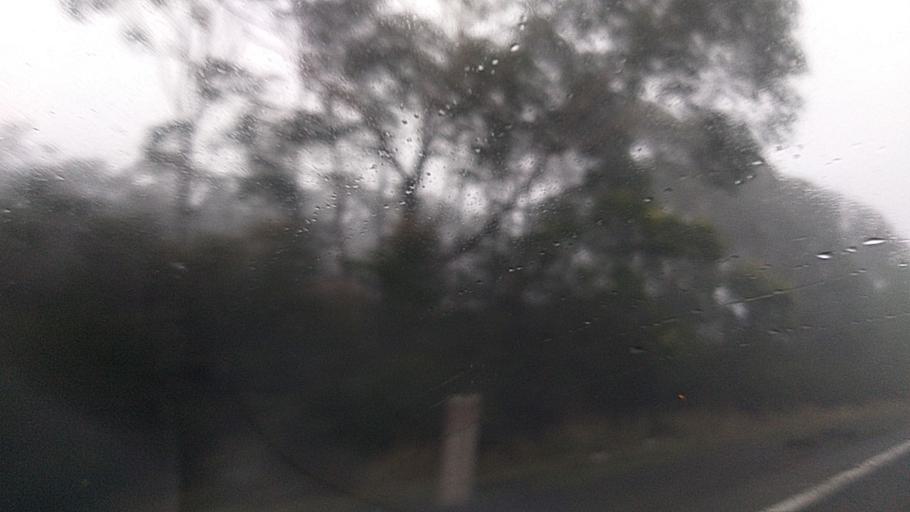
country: AU
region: New South Wales
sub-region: Wollondilly
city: Douglas Park
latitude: -34.3179
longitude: 150.7538
